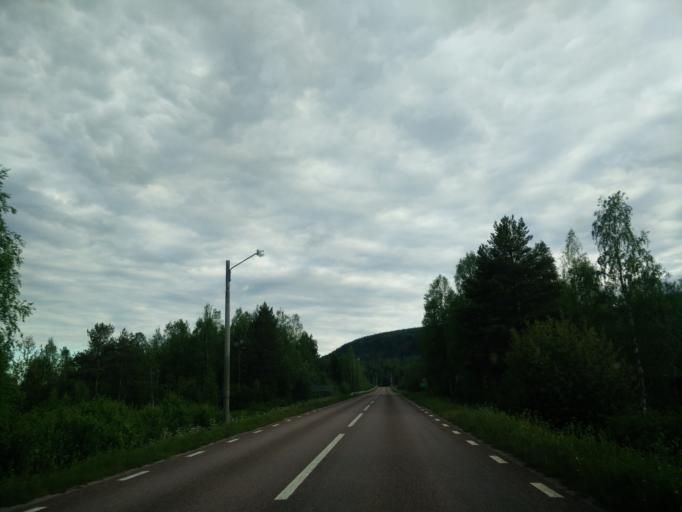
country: SE
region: Jaemtland
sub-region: Harjedalens Kommun
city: Sveg
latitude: 62.2768
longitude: 14.8063
